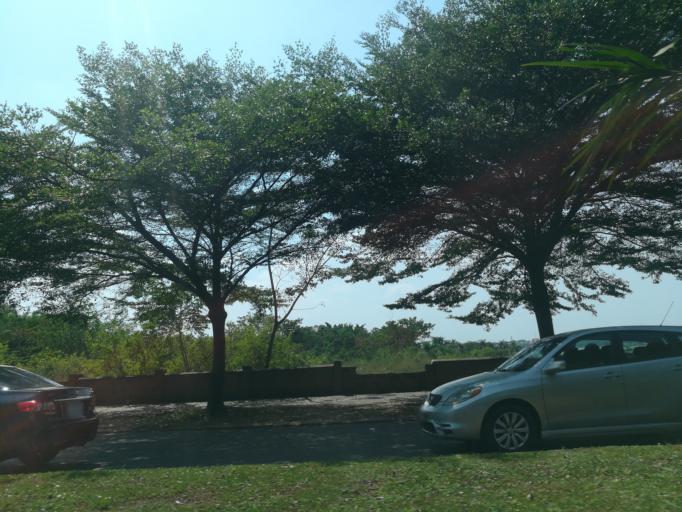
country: NG
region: Abuja Federal Capital Territory
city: Abuja
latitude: 9.0738
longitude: 7.4288
